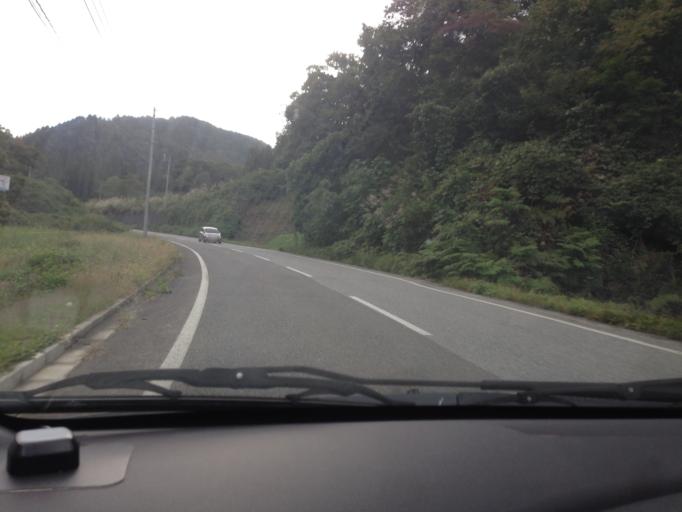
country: JP
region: Fukushima
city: Kitakata
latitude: 37.4742
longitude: 139.6896
